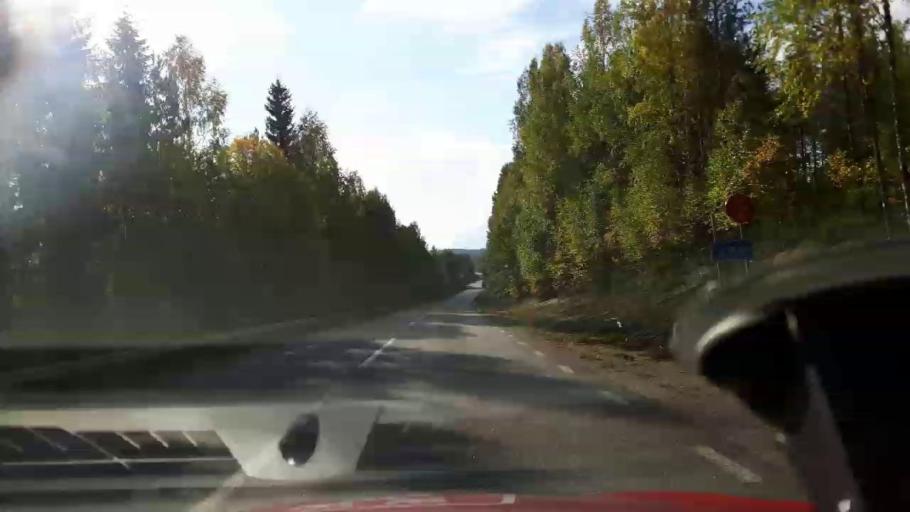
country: SE
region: Vaesternorrland
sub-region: Ange Kommun
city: Ange
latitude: 62.0781
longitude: 15.1001
